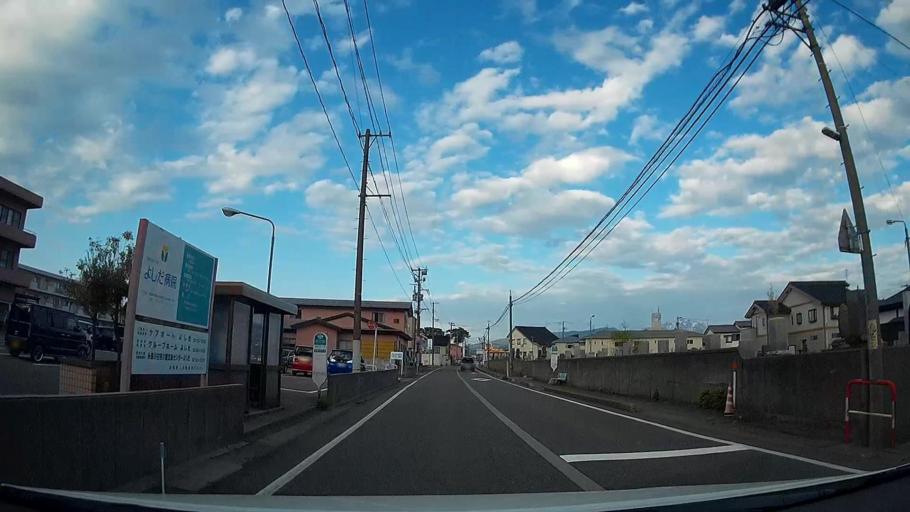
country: JP
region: Niigata
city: Itoigawa
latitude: 37.0426
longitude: 137.8476
